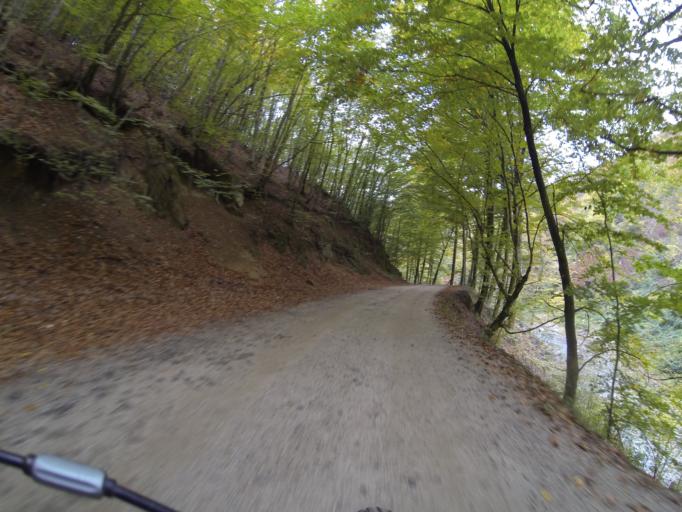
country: RO
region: Gorj
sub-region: Comuna Tismana
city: Sohodol
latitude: 45.0612
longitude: 22.8972
